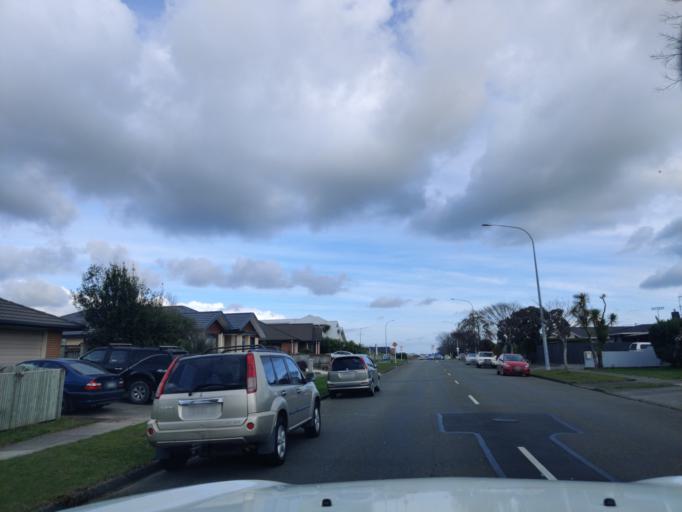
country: NZ
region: Manawatu-Wanganui
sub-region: Palmerston North City
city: Palmerston North
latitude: -40.3356
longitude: 175.6078
